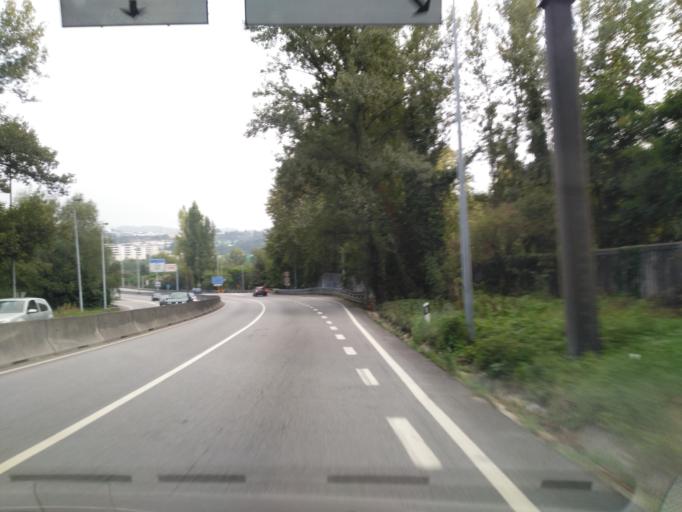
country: PT
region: Braga
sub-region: Guimaraes
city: Guimaraes
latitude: 41.4413
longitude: -8.3078
